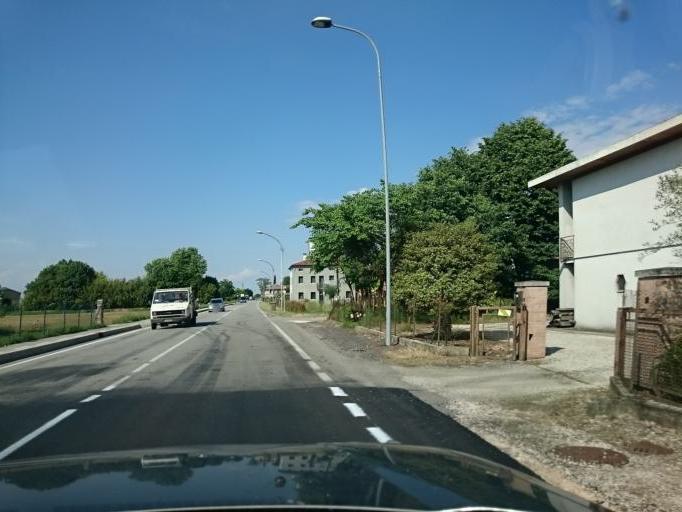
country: IT
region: Veneto
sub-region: Provincia di Vicenza
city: Montegalda
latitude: 45.4524
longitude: 11.6849
